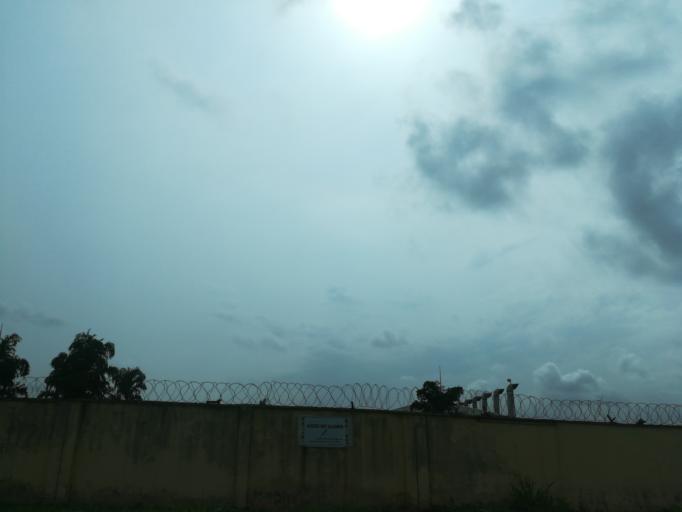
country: NG
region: Lagos
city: Oshodi
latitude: 6.5682
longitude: 3.3235
